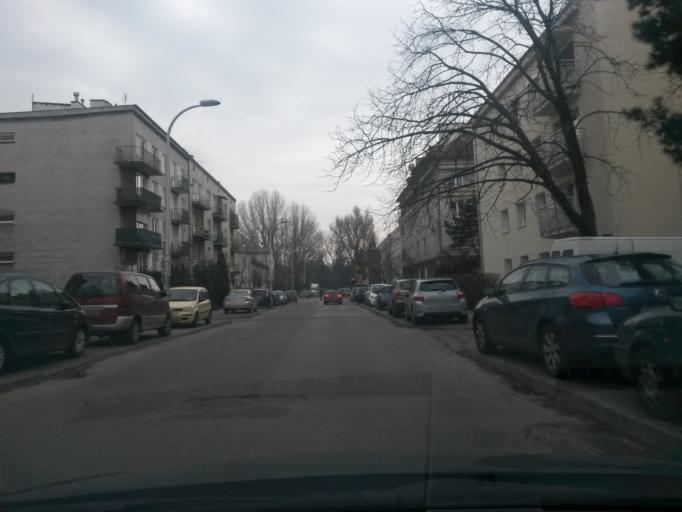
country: PL
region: Masovian Voivodeship
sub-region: Warszawa
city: Mokotow
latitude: 52.2029
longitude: 21.0394
